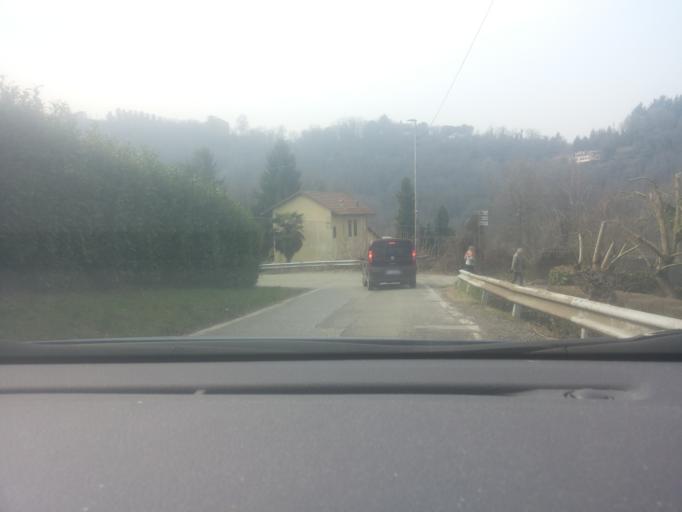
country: IT
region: Piedmont
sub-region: Provincia di Torino
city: Turin
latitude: 45.0575
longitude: 7.7209
